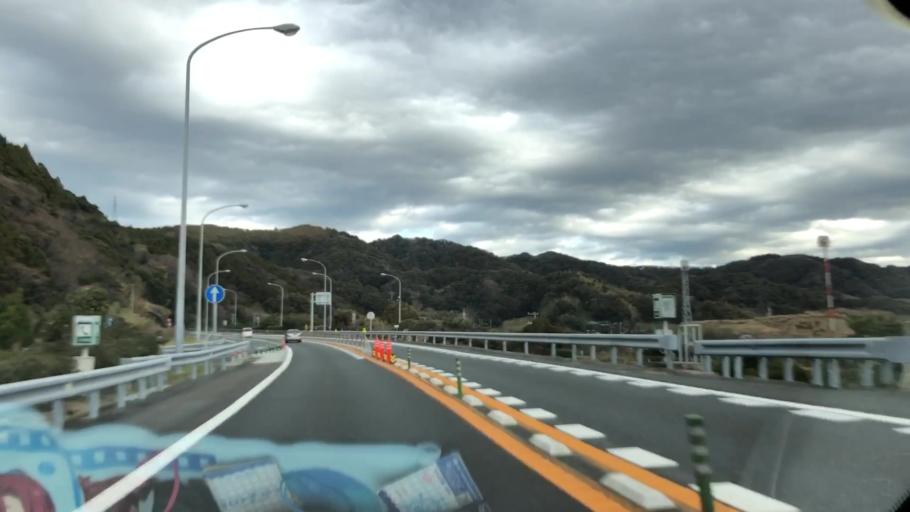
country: JP
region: Chiba
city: Tateyama
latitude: 35.1149
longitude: 139.8514
